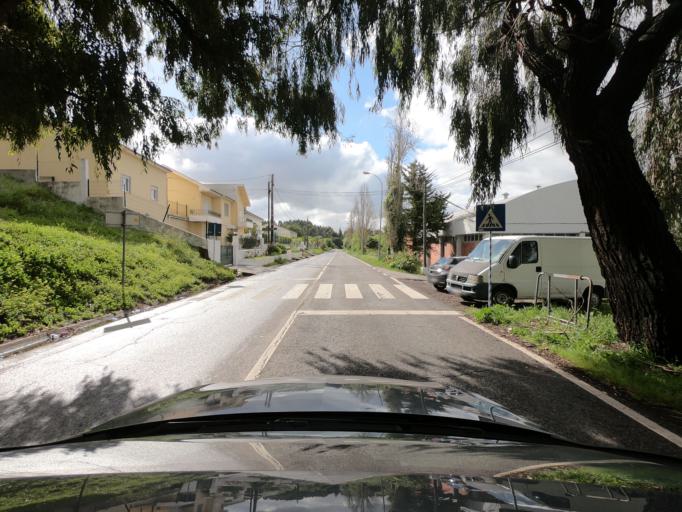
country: PT
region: Lisbon
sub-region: Oeiras
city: Quejas
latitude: 38.7307
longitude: -9.2584
